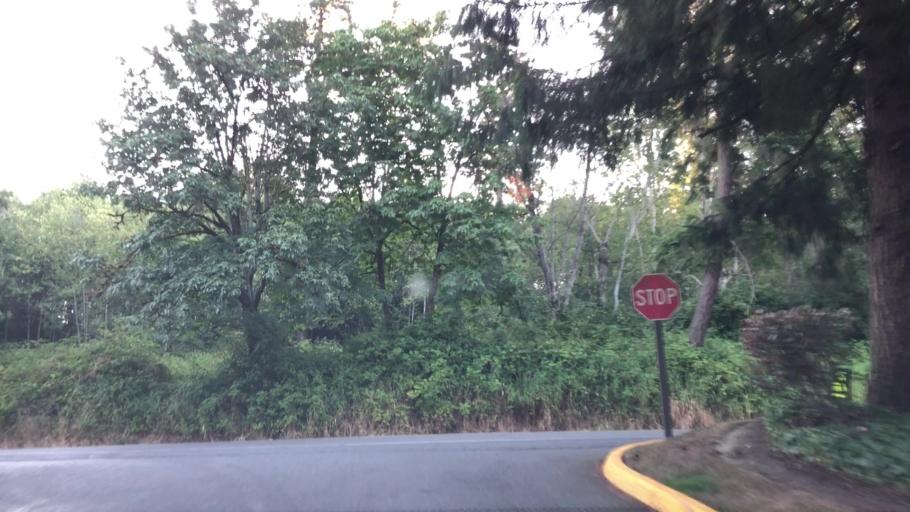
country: US
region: Washington
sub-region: King County
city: Lea Hill
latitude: 47.3139
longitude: -122.2002
